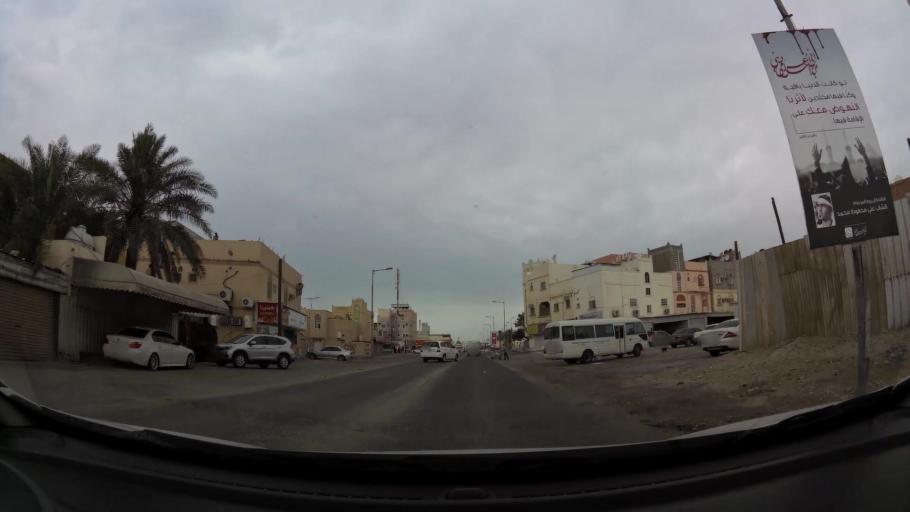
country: BH
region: Central Governorate
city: Madinat Hamad
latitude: 26.1234
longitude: 50.4776
